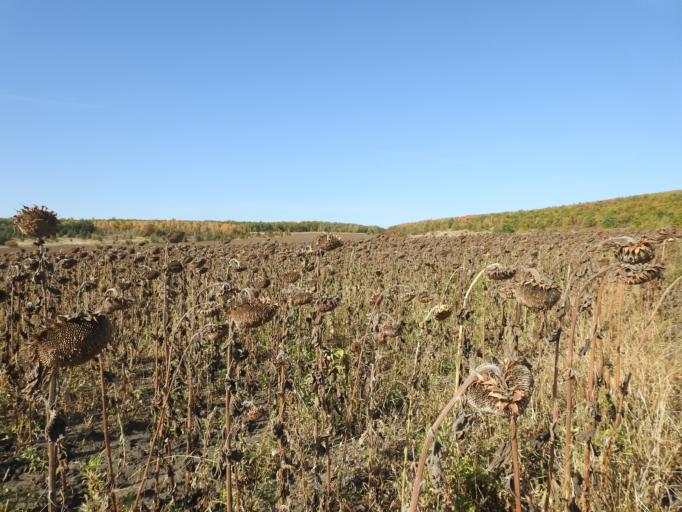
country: RU
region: Saratov
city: Baltay
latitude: 52.4792
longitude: 46.7055
